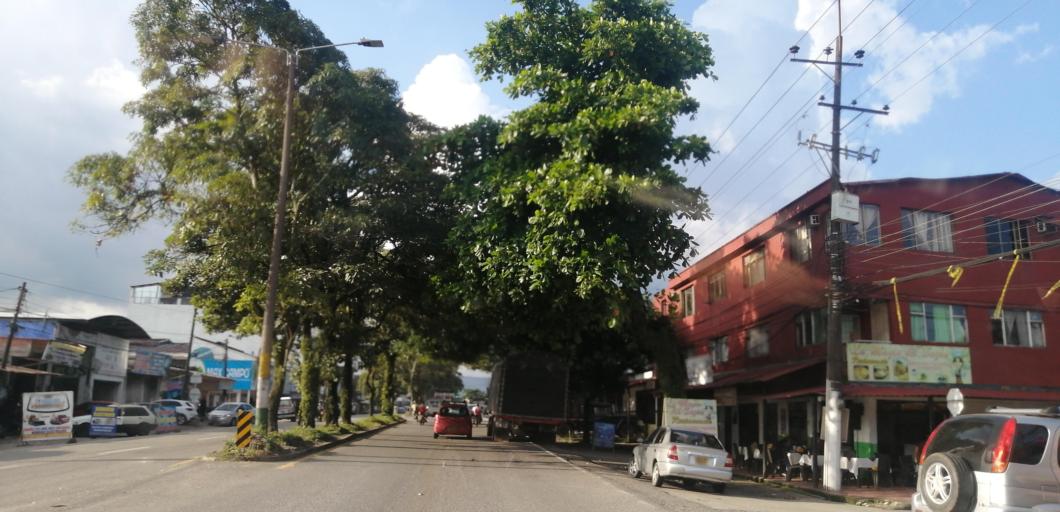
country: CO
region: Meta
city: Acacias
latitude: 3.9819
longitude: -73.7667
